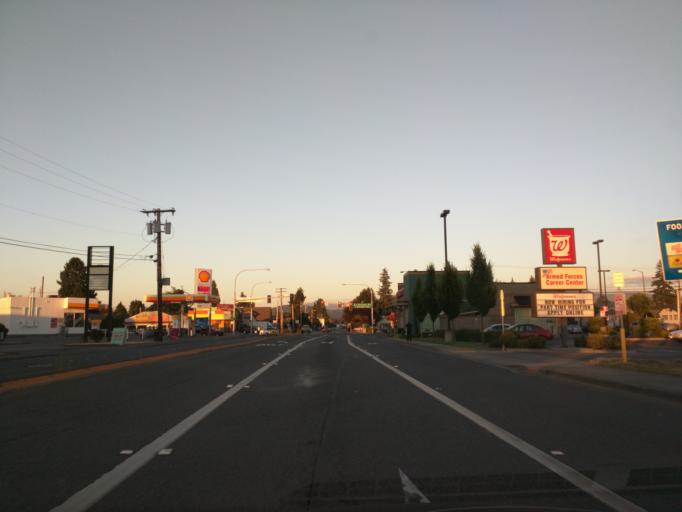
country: US
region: Washington
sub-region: Skagit County
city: Burlington
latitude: 48.4717
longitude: -122.3372
